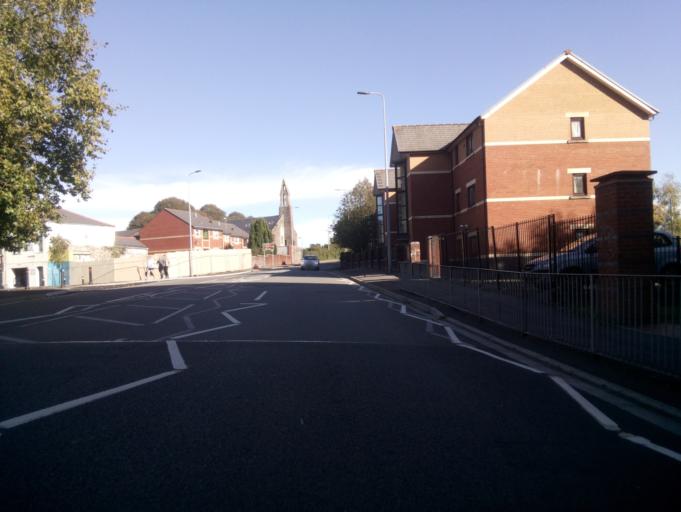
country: GB
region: Wales
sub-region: Cardiff
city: Cardiff
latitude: 51.4807
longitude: -3.1641
